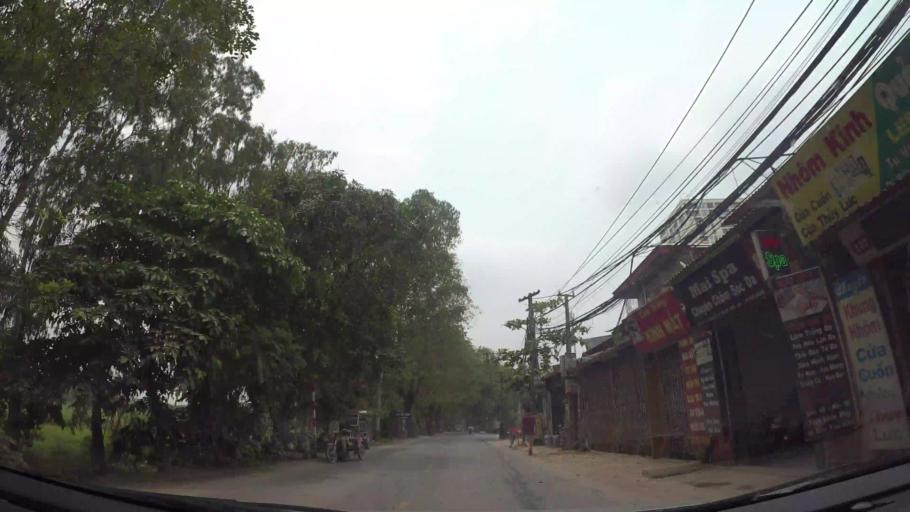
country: VN
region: Ha Noi
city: Cau Dien
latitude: 21.0152
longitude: 105.7456
